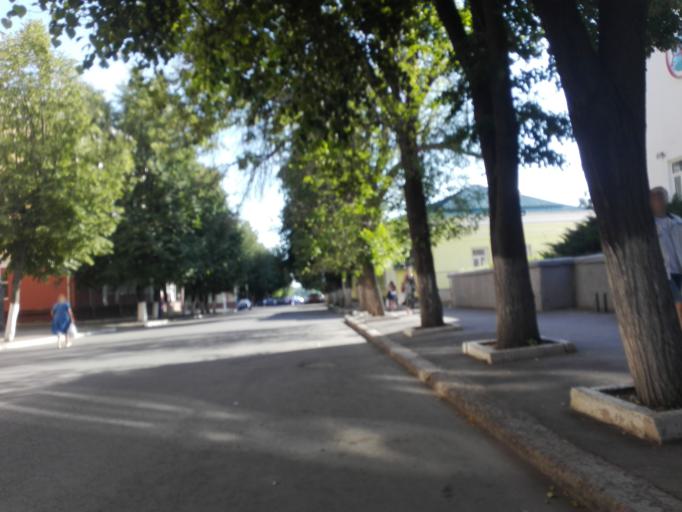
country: RU
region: Orjol
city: Orel
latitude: 52.9695
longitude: 36.0547
